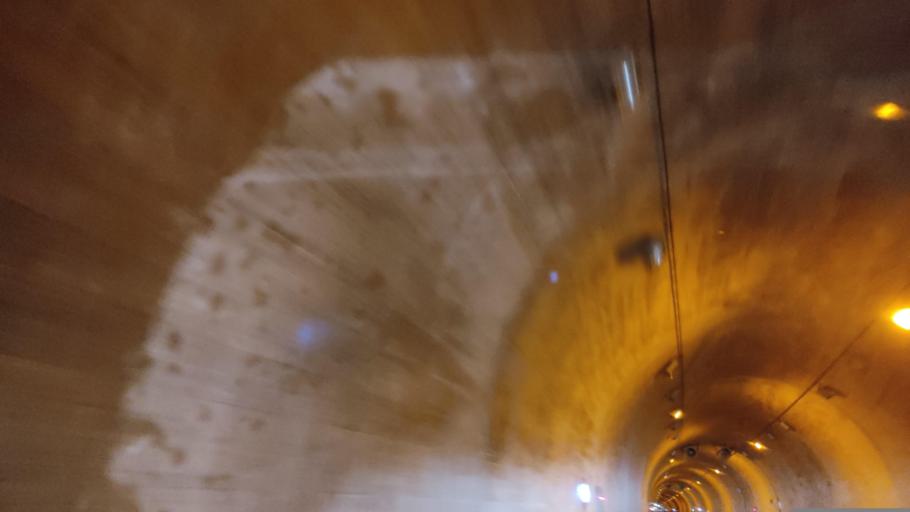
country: JP
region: Iwate
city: Shizukuishi
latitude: 39.6317
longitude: 141.0548
